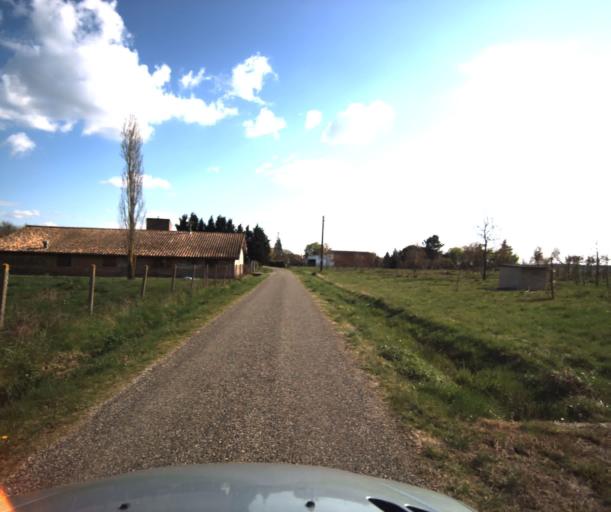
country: FR
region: Midi-Pyrenees
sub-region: Departement du Tarn-et-Garonne
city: Bressols
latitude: 43.9680
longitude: 1.2956
